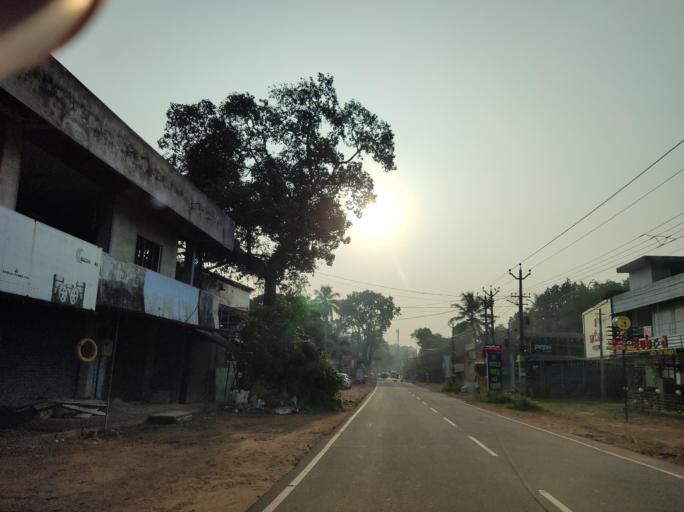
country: IN
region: Kerala
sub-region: Alappuzha
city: Kattanam
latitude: 9.1756
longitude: 76.6335
